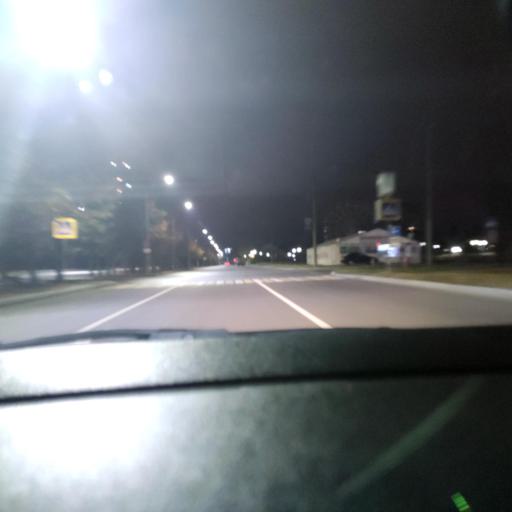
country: RU
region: Voronezj
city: Podgornoye
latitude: 51.7105
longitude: 39.1624
